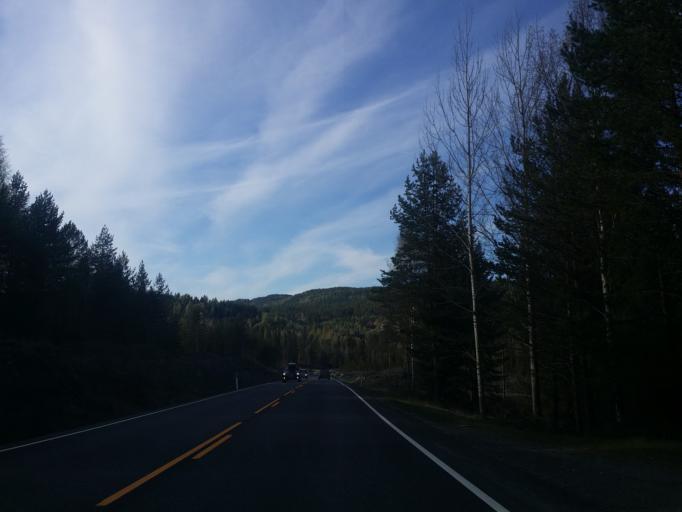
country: NO
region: Buskerud
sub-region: Kongsberg
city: Kongsberg
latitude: 59.6207
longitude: 9.4744
